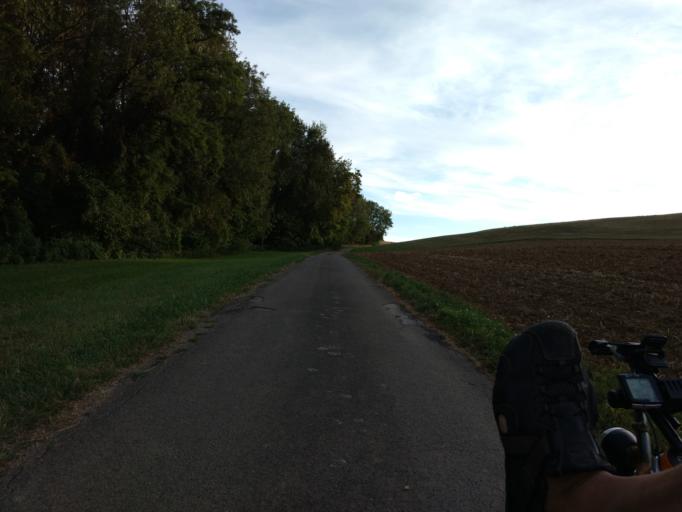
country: DE
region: Saarland
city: Merzig
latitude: 49.4075
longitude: 6.6148
